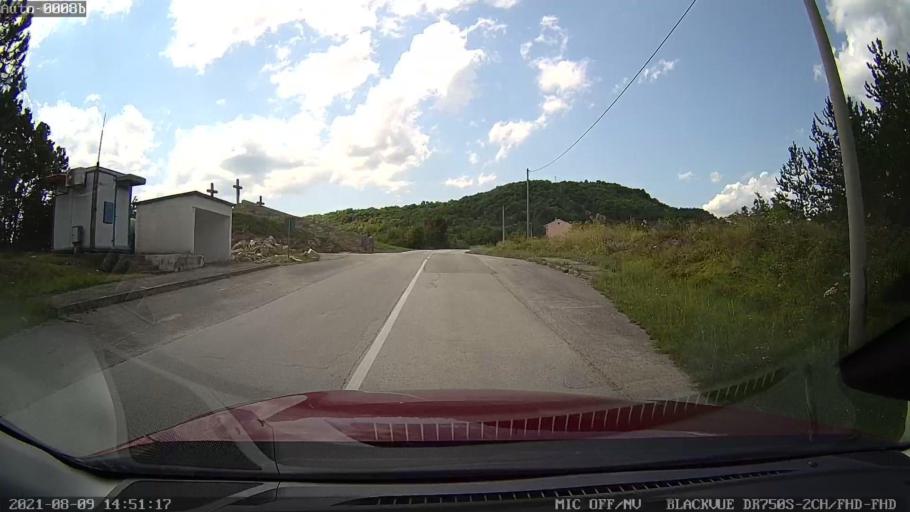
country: HR
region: Istarska
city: Pazin
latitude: 45.2907
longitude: 14.0915
